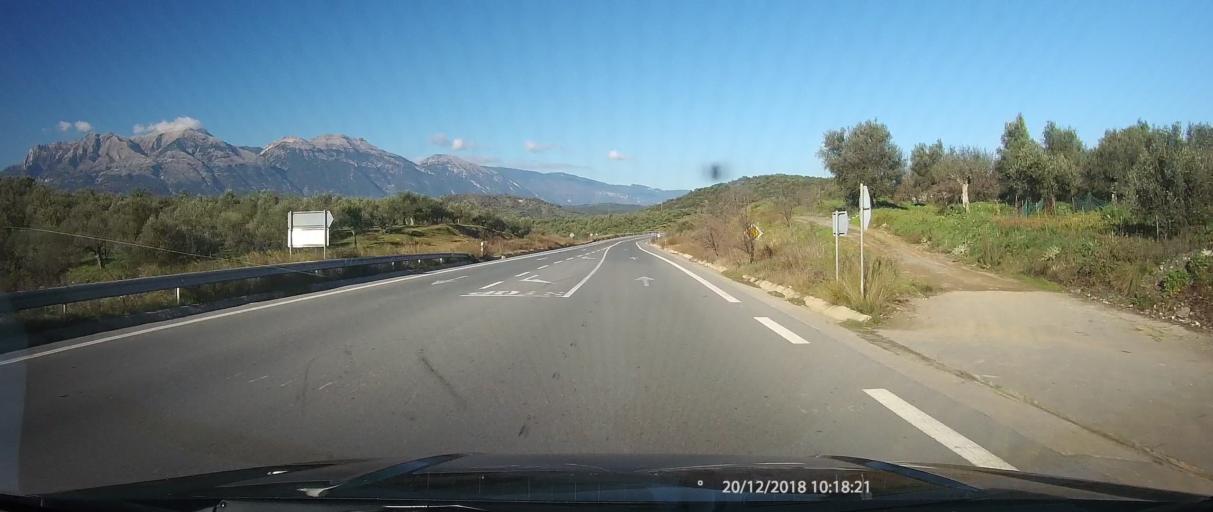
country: GR
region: Peloponnese
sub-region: Nomos Lakonias
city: Magoula
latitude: 37.1160
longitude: 22.4252
